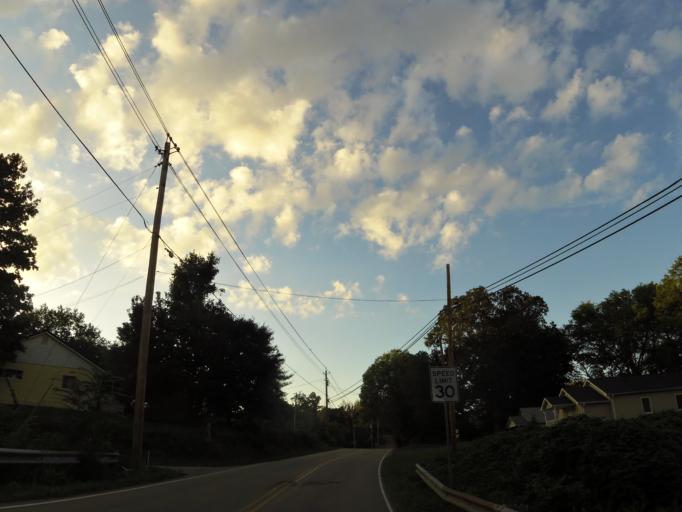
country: US
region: Tennessee
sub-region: Knox County
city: Farragut
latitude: 35.9082
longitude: -84.1710
